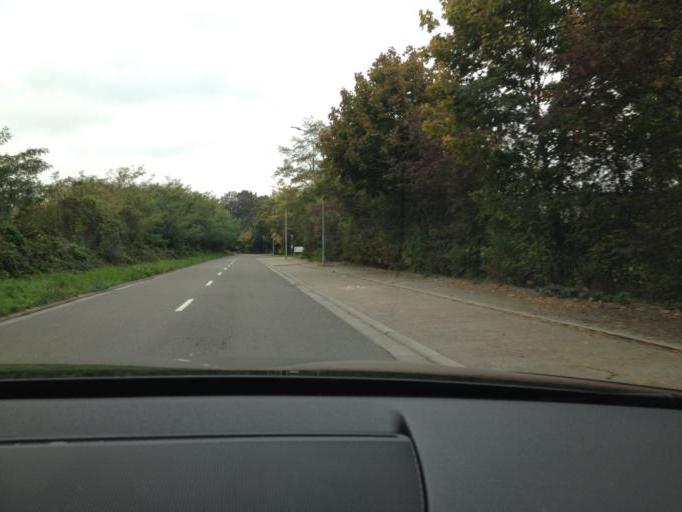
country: DE
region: Rheinland-Pfalz
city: Speyer
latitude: 49.3377
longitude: 8.4145
